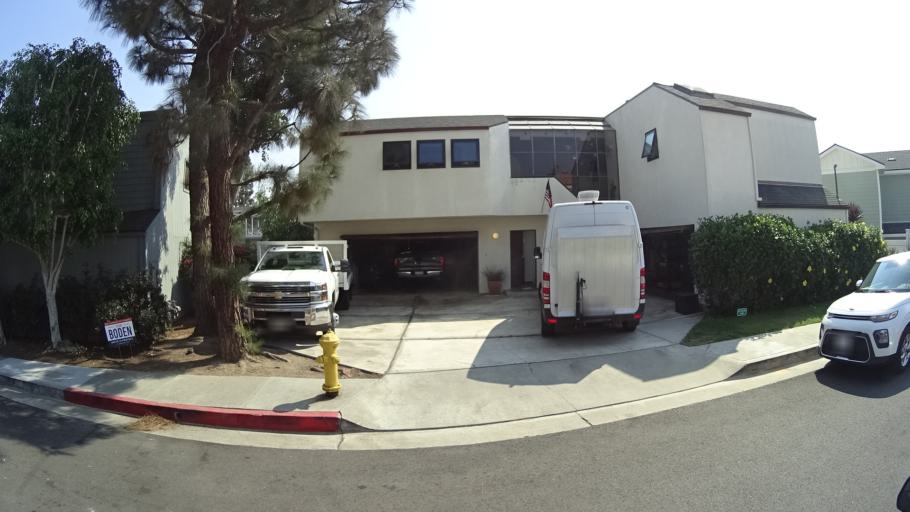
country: US
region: California
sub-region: Orange County
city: San Clemente
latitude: 33.4197
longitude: -117.6155
